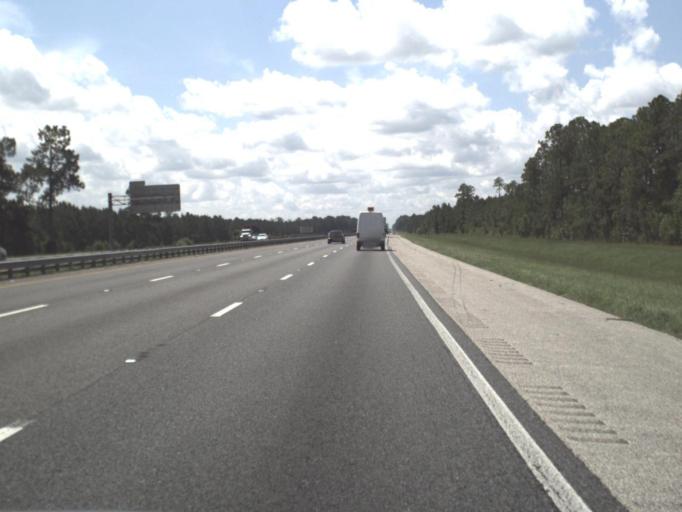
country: US
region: Florida
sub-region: Saint Johns County
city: Saint Augustine Shores
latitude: 29.8088
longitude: -81.3712
